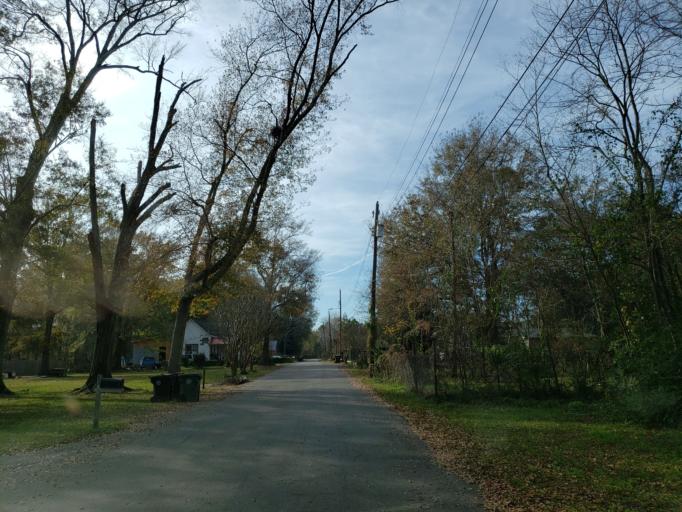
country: US
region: Mississippi
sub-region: Forrest County
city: Hattiesburg
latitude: 31.3345
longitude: -89.3065
